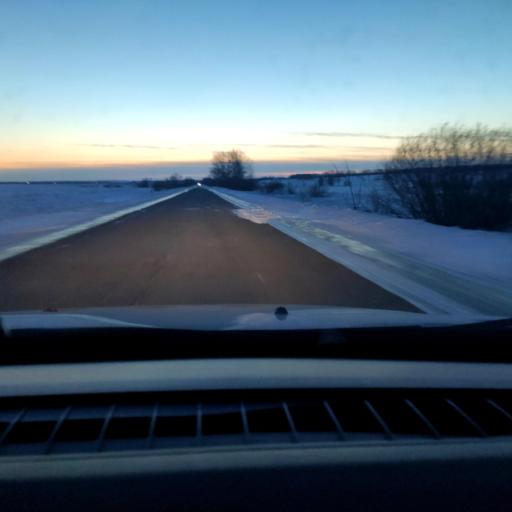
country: RU
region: Samara
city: Georgiyevka
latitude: 53.3382
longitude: 50.9512
